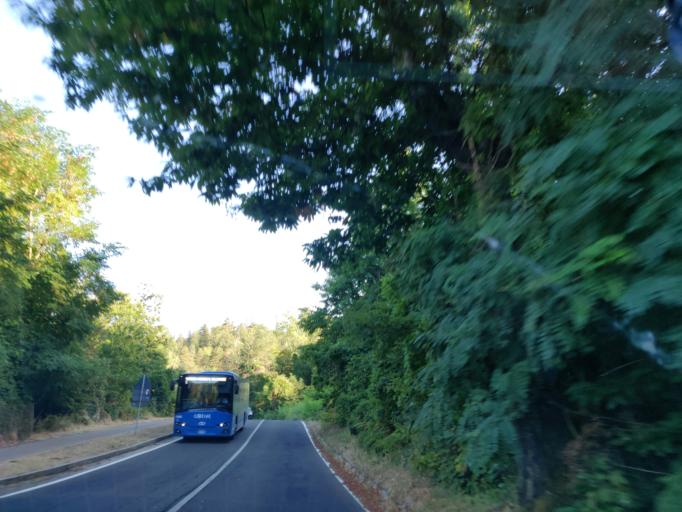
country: IT
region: Tuscany
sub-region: Provincia di Siena
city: Piancastagnaio
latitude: 42.8624
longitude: 11.6788
